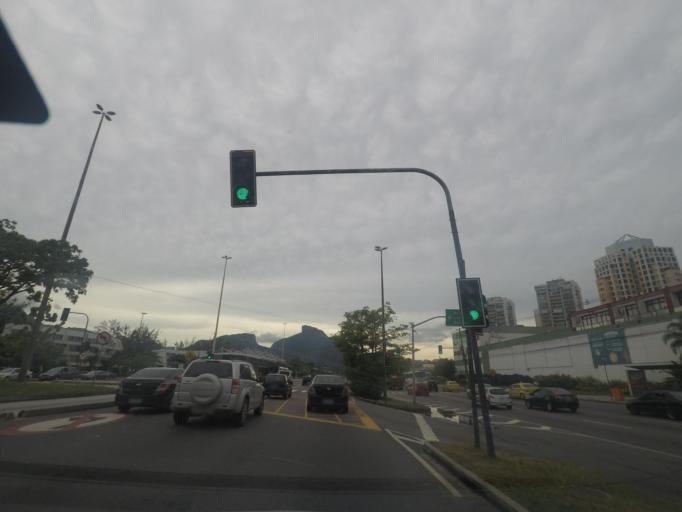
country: BR
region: Rio de Janeiro
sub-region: Rio De Janeiro
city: Rio de Janeiro
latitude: -23.0005
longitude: -43.3430
